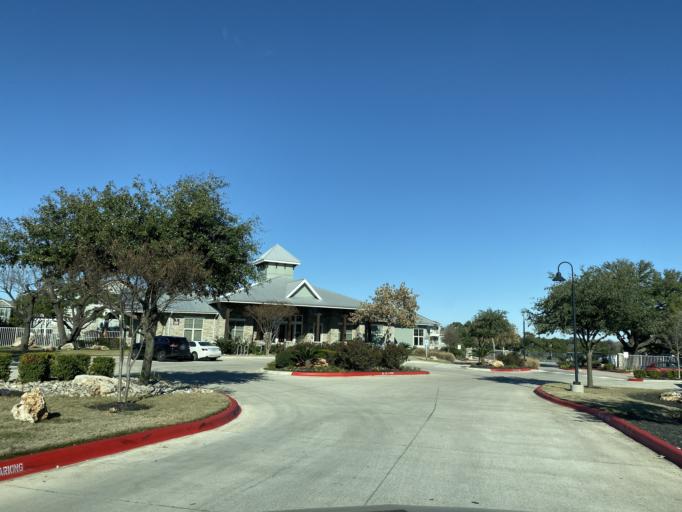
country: US
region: Texas
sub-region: Williamson County
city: Jollyville
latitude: 30.4813
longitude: -97.7685
